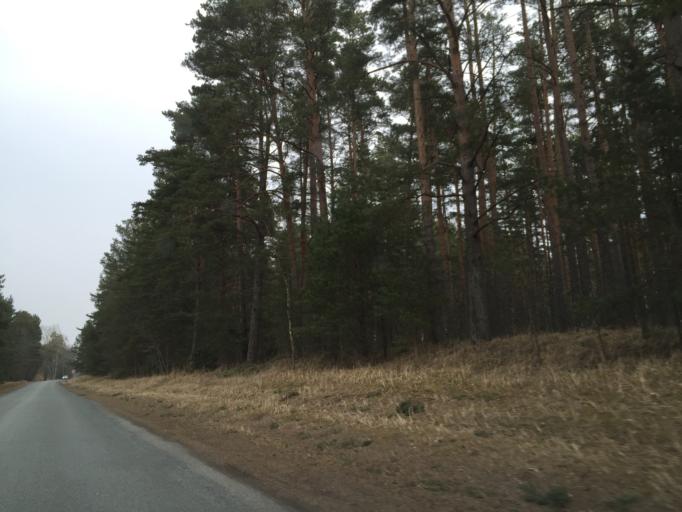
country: LV
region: Salacgrivas
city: Ainazi
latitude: 57.9936
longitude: 24.4285
